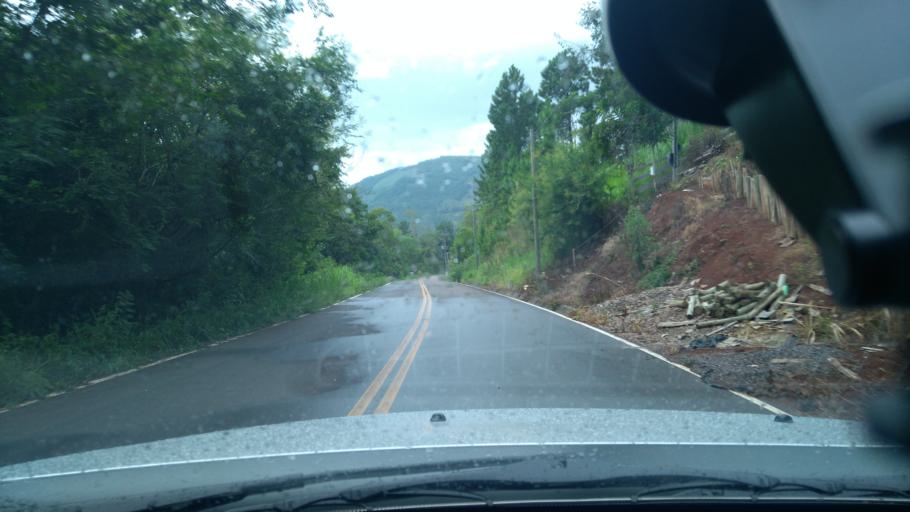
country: BR
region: Rio Grande do Sul
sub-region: Torres
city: Torres
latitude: -29.1980
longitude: -49.9713
